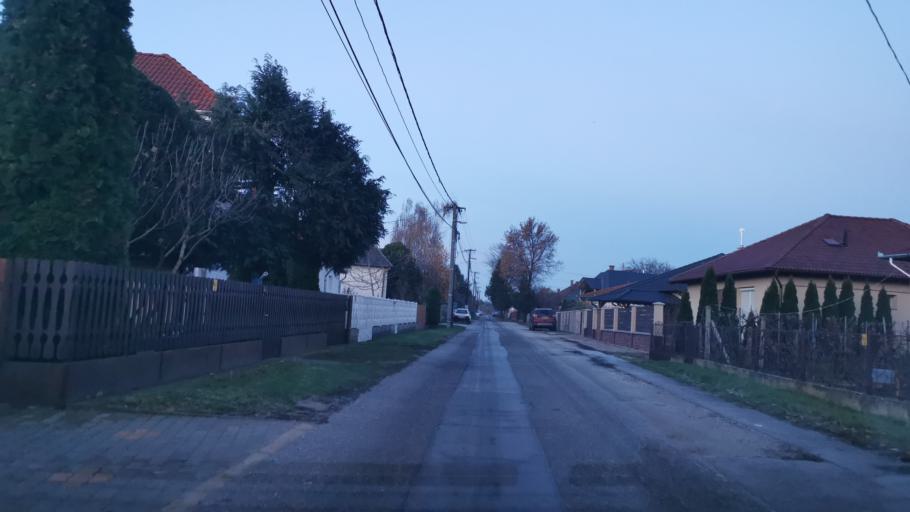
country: HU
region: Hajdu-Bihar
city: Debrecen
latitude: 47.5929
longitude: 21.5679
